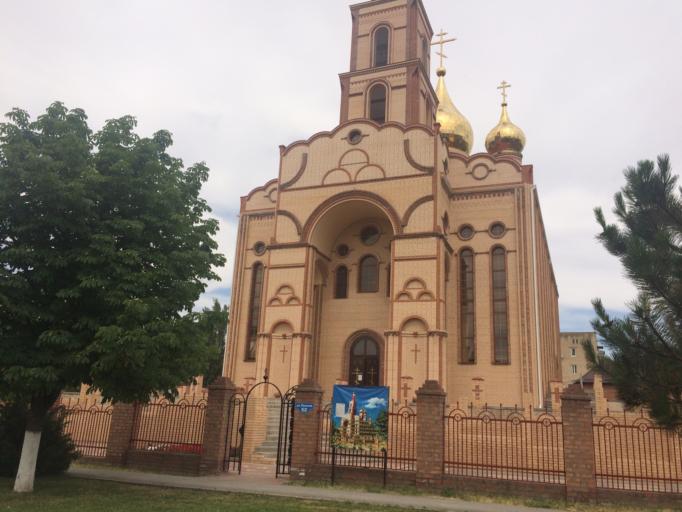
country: RU
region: Rostov
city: Sal'sk
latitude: 46.4802
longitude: 41.5375
